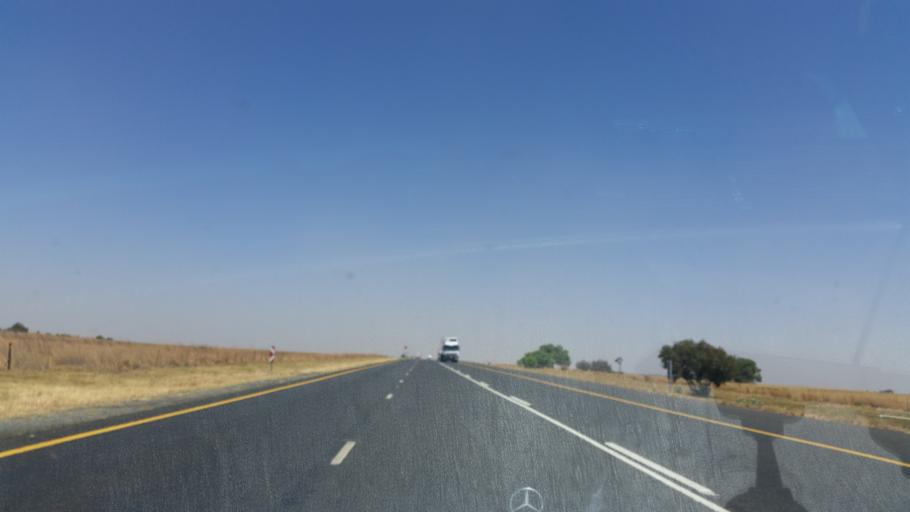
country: ZA
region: Orange Free State
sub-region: Lejweleputswa District Municipality
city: Winburg
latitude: -28.6439
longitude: 26.8855
